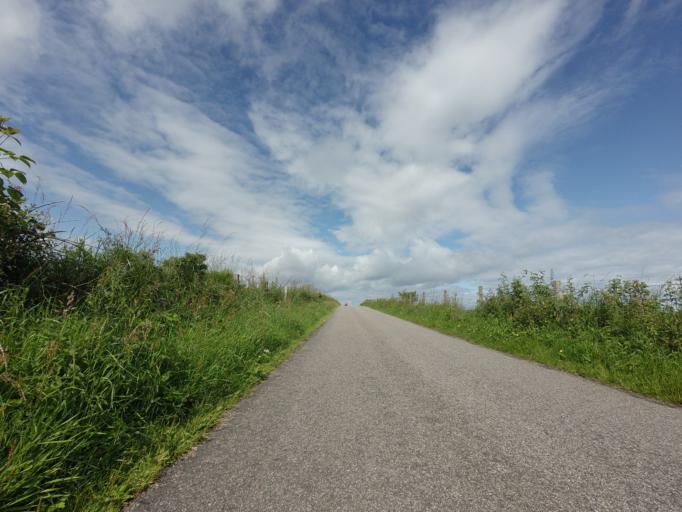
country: GB
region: Scotland
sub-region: Moray
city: Burghead
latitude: 57.6540
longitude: -3.4722
